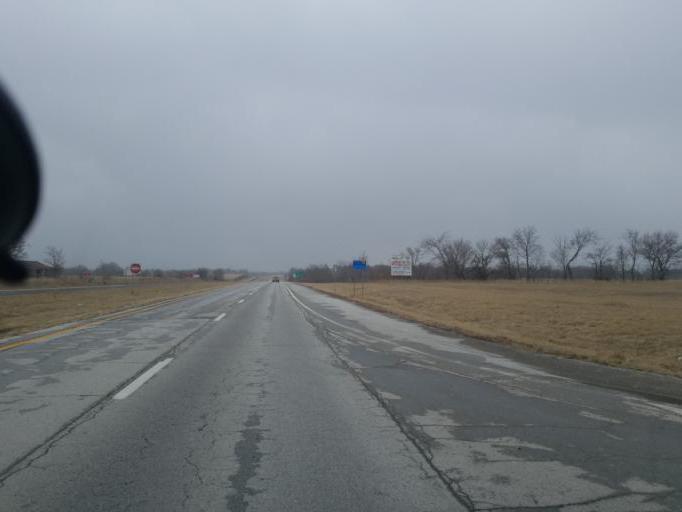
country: US
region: Missouri
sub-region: Macon County
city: La Plata
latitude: 39.8986
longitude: -92.4722
